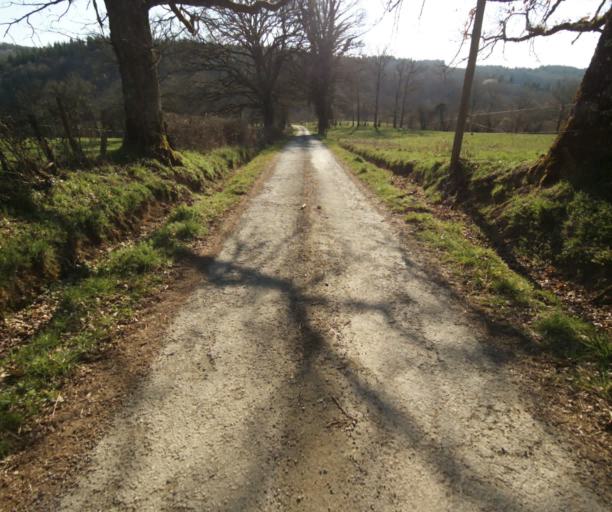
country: FR
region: Limousin
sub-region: Departement de la Correze
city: Chamboulive
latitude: 45.4943
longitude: 1.7278
